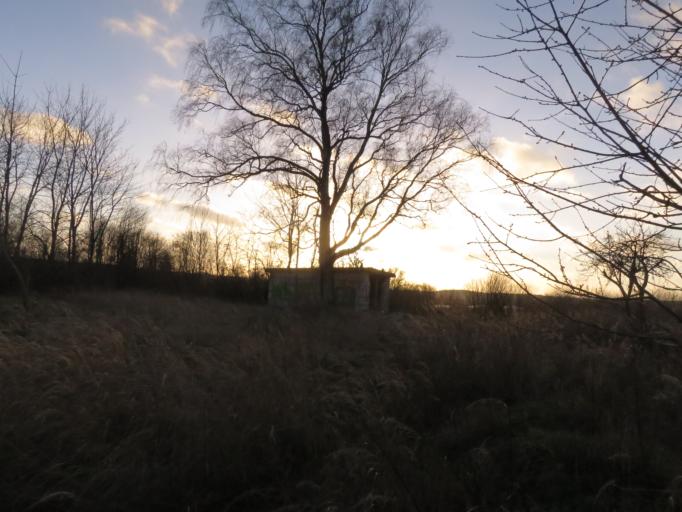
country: LV
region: Riga
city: Bergi
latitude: 56.9736
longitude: 24.3067
